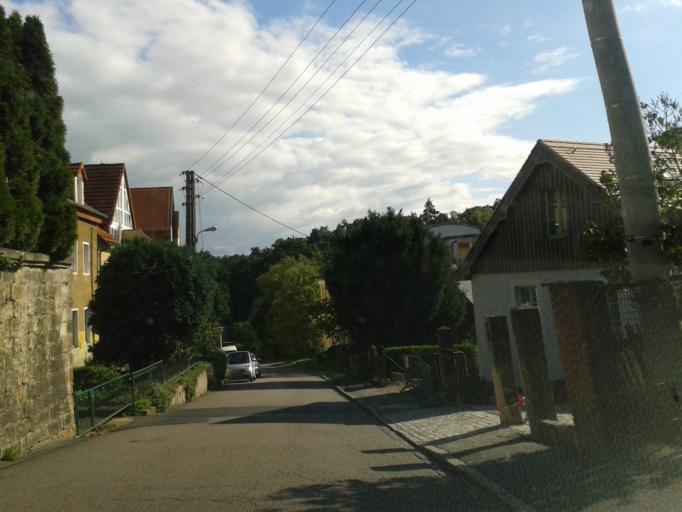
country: DE
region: Saxony
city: Albertstadt
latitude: 51.0617
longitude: 13.8249
